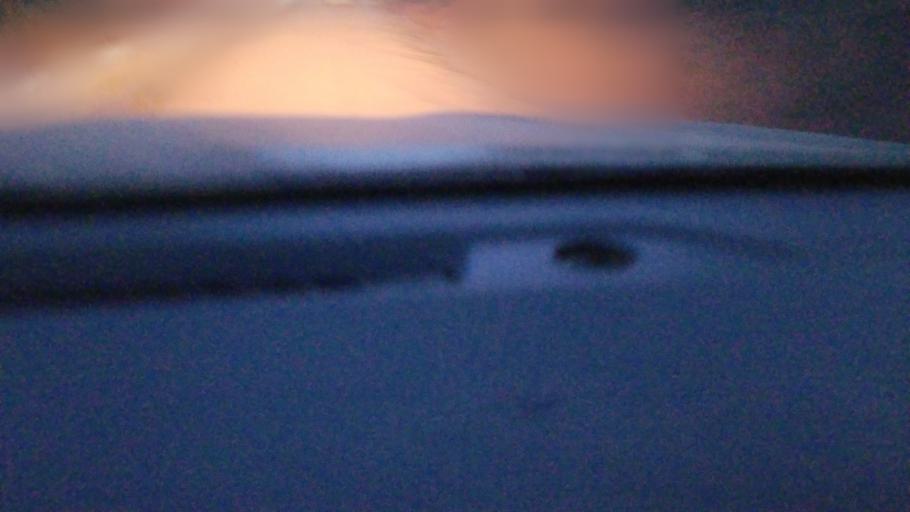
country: NG
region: Enugu
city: Obollo-Afor
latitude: 6.9035
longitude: 7.5099
